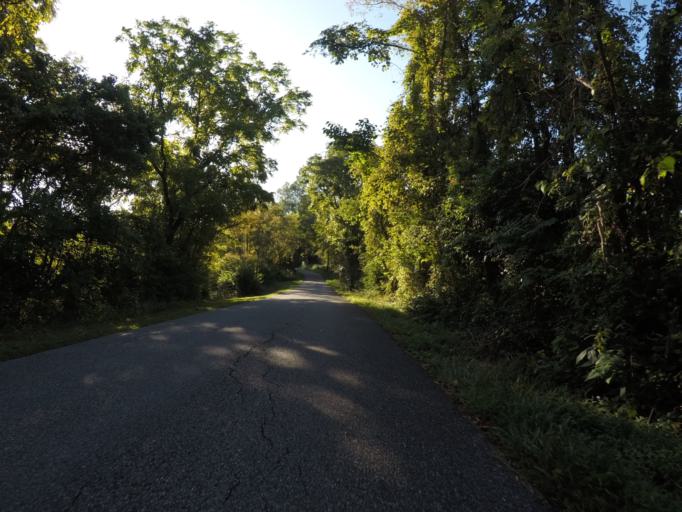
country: US
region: Ohio
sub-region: Lawrence County
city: Coal Grove
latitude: 38.5978
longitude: -82.5530
